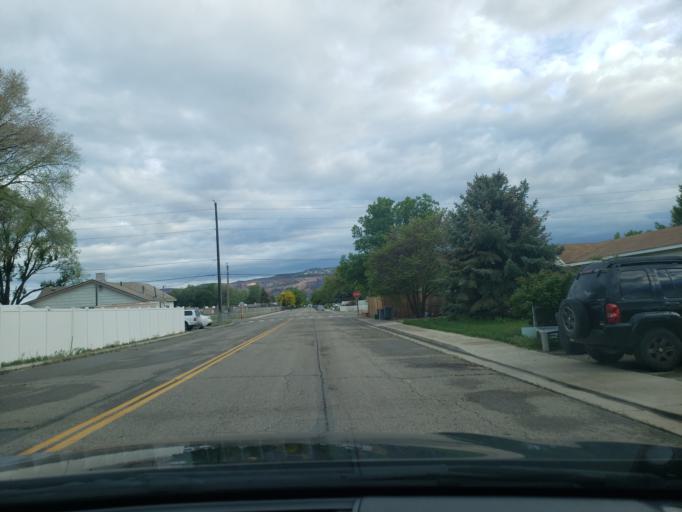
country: US
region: Colorado
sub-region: Mesa County
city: Fruita
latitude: 39.1650
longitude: -108.7314
